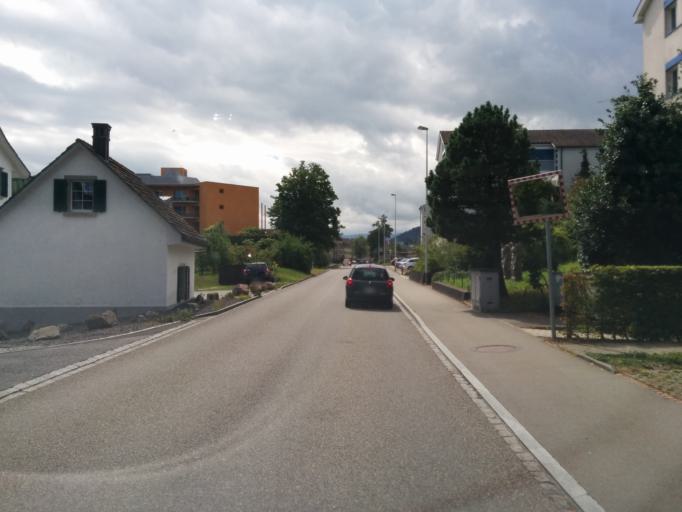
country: CH
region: Zurich
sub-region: Bezirk Horgen
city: Oberrieden / Mitte
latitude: 47.2687
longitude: 8.5827
